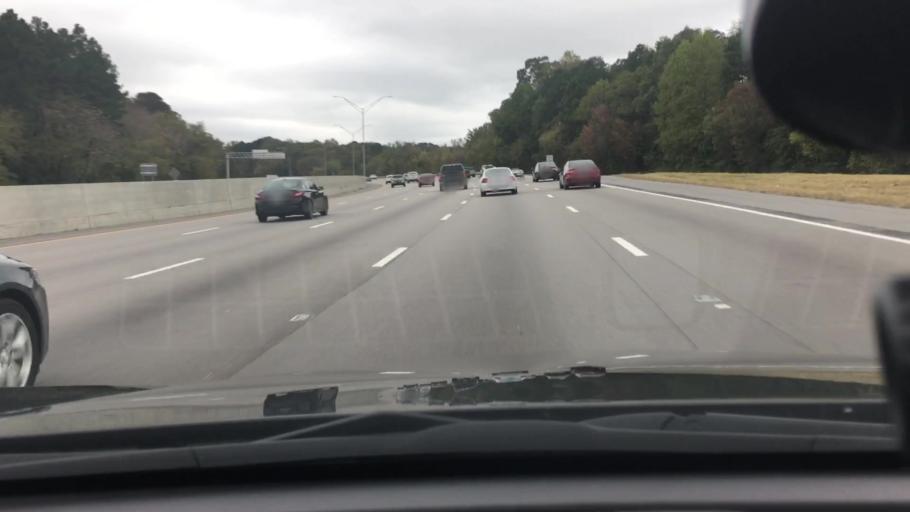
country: US
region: North Carolina
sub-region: Wake County
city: Raleigh
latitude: 35.7576
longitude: -78.6154
